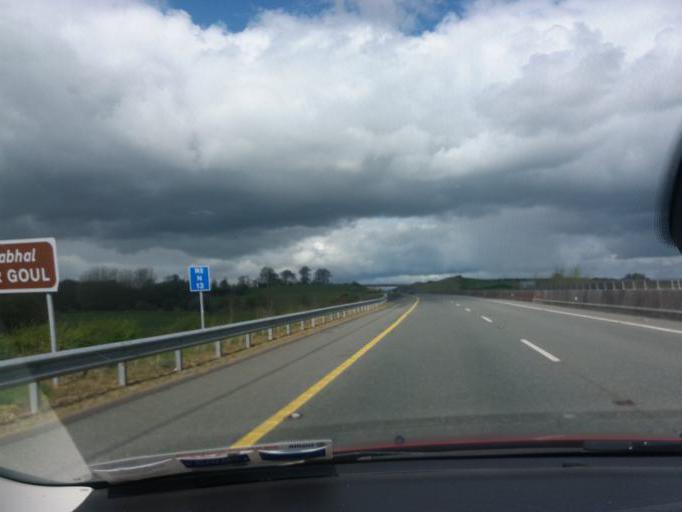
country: IE
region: Leinster
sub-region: Laois
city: Rathdowney
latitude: 52.8185
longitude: -7.4938
